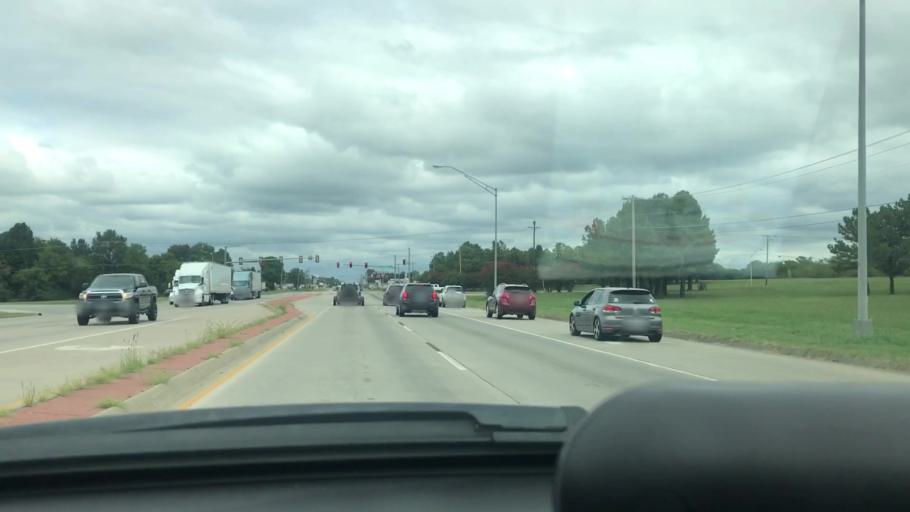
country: US
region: Oklahoma
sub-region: Muskogee County
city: Muskogee
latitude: 35.7678
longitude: -95.4024
